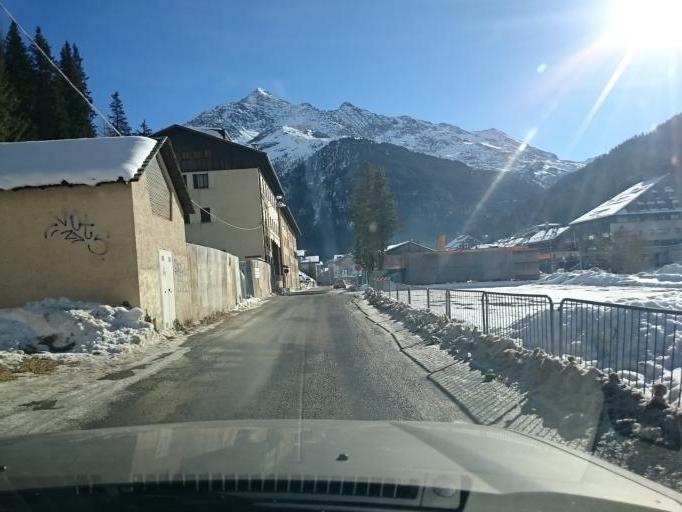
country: IT
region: Lombardy
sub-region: Provincia di Sondrio
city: Sant'Antonio
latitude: 46.4140
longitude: 10.4928
